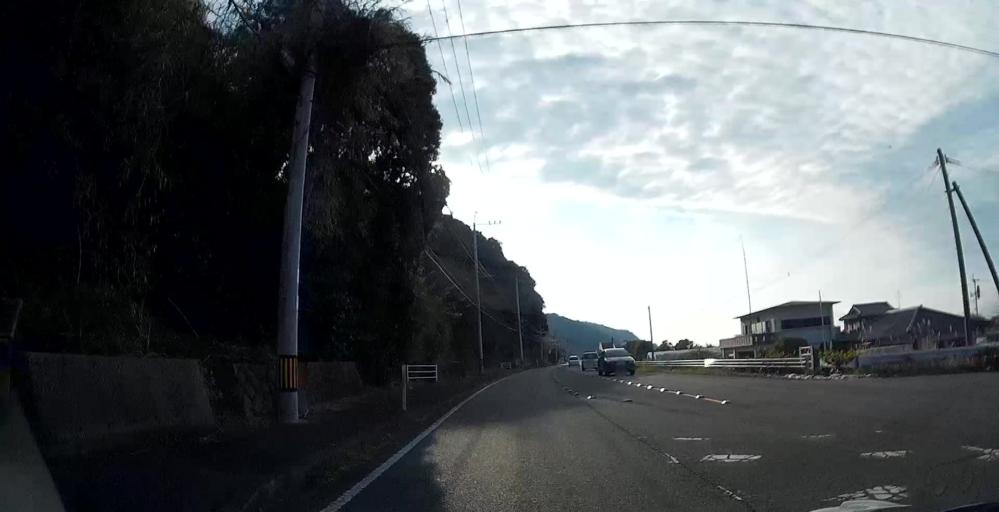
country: JP
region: Kumamoto
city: Matsubase
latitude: 32.6587
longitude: 130.5169
